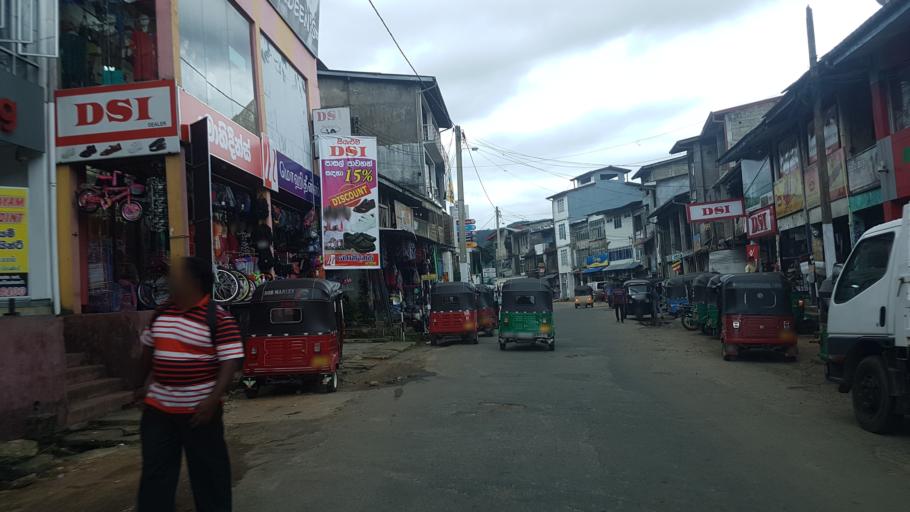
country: LK
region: Western
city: Hanwella Ihala
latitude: 7.0288
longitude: 80.2956
